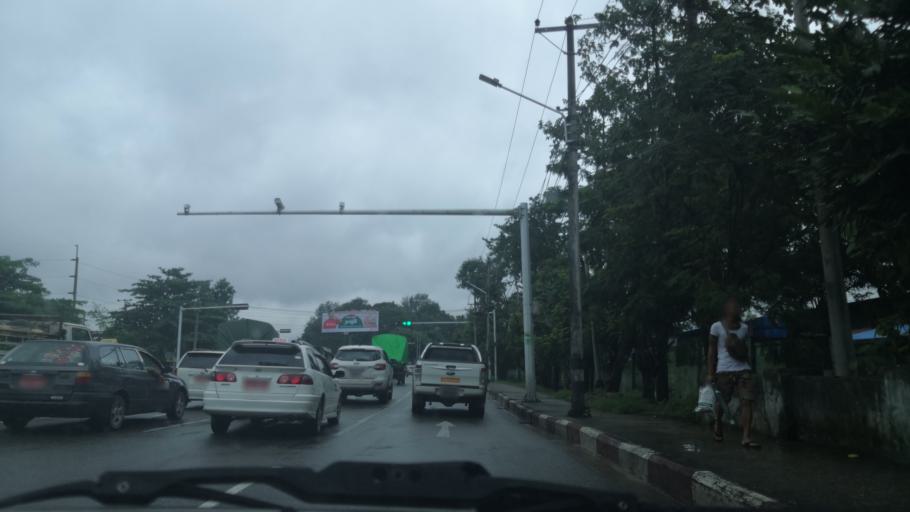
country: MM
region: Yangon
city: Yangon
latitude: 16.8895
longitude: 96.1218
